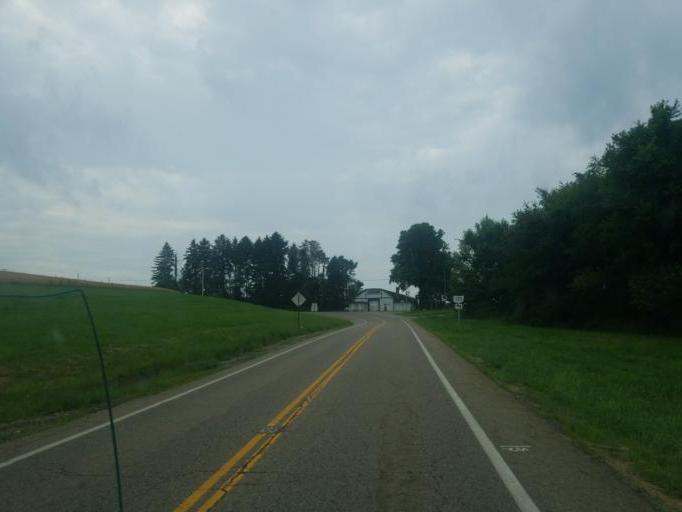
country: US
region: Ohio
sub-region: Carroll County
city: Lake Mohawk
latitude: 40.6522
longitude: -81.2380
